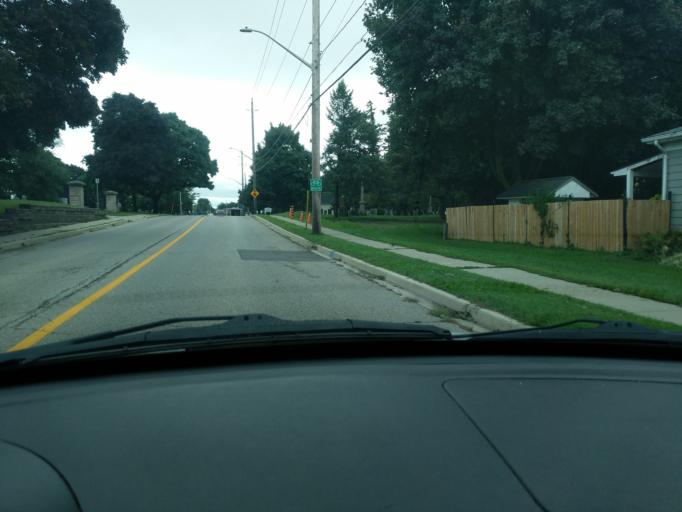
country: CA
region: Ontario
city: Cambridge
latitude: 43.4285
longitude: -80.2988
